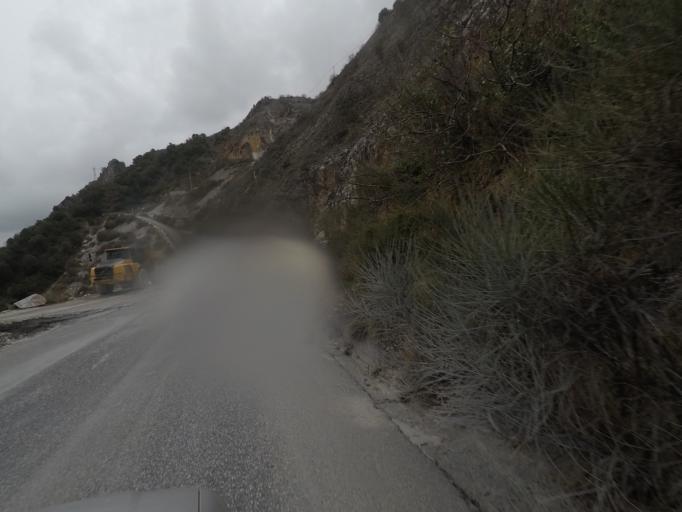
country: IT
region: Tuscany
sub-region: Provincia di Massa-Carrara
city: Massa
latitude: 44.0801
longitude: 10.1340
